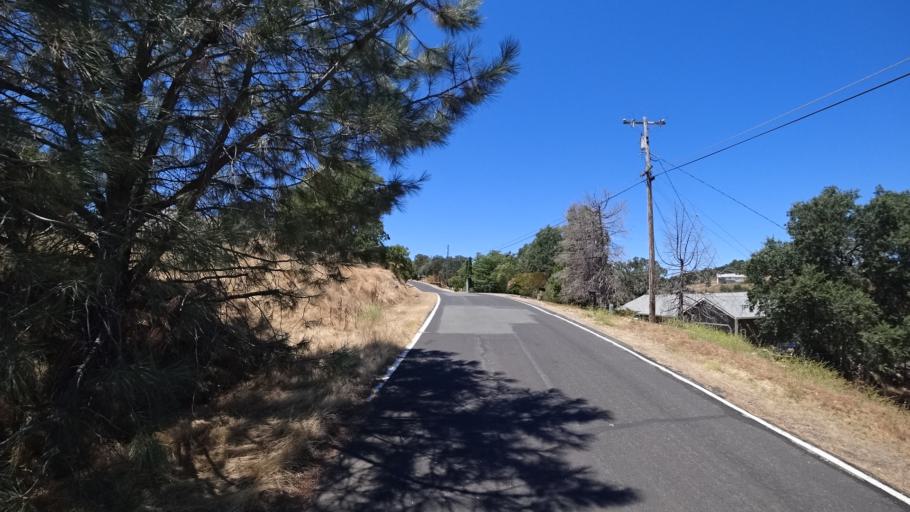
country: US
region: California
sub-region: Calaveras County
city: Rancho Calaveras
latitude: 38.1454
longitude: -120.8394
